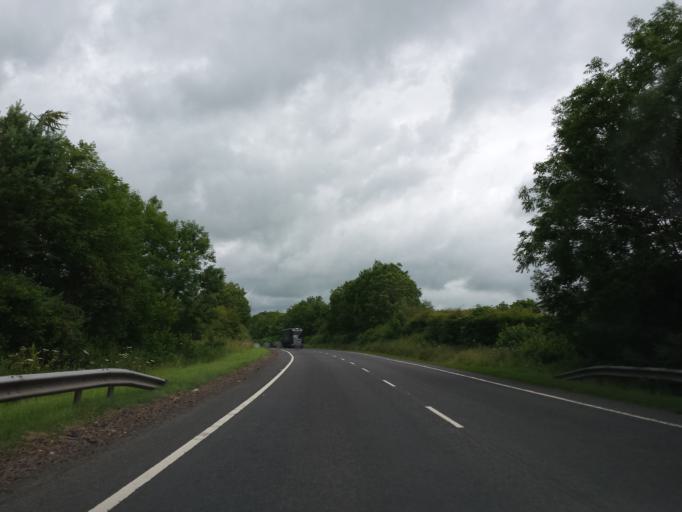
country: GB
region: Scotland
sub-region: Dumfries and Galloway
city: Castle Douglas
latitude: 54.9513
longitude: -3.9287
